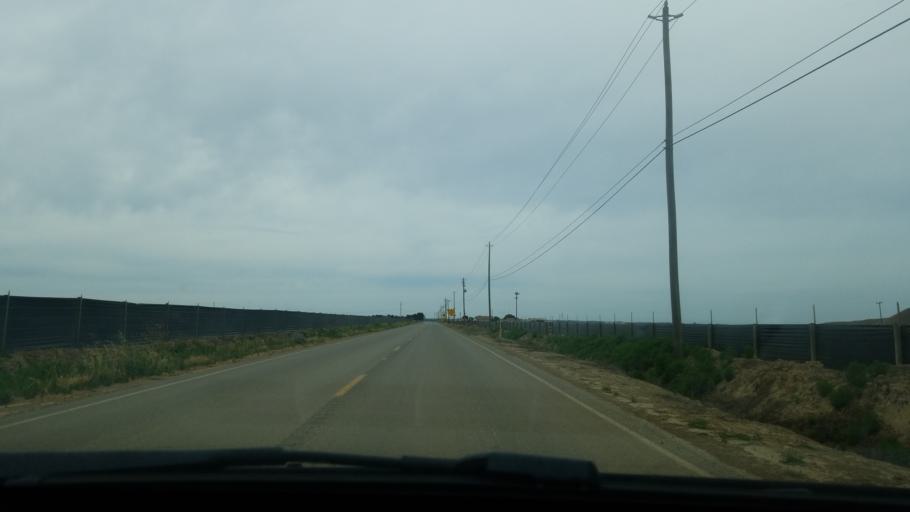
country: US
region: California
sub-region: San Luis Obispo County
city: Nipomo
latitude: 35.0044
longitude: -120.5142
